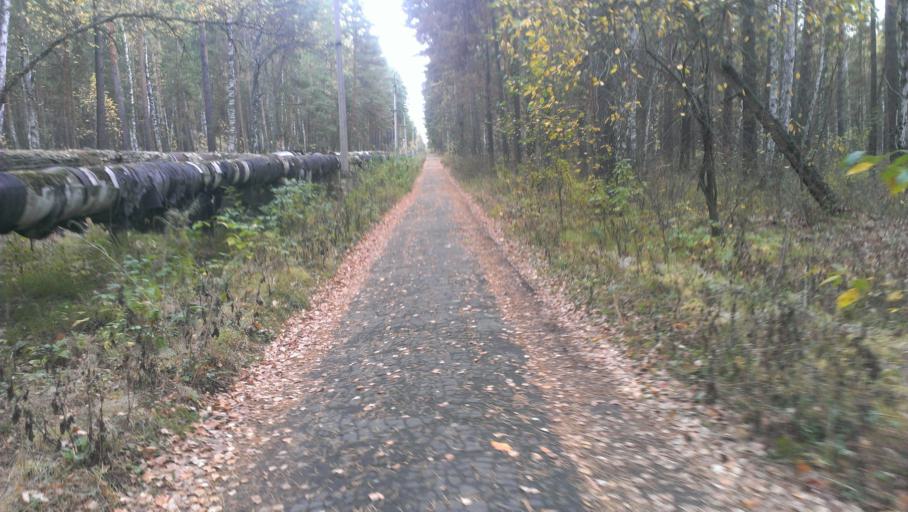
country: RU
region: Altai Krai
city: Yuzhnyy
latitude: 53.2682
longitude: 83.6825
